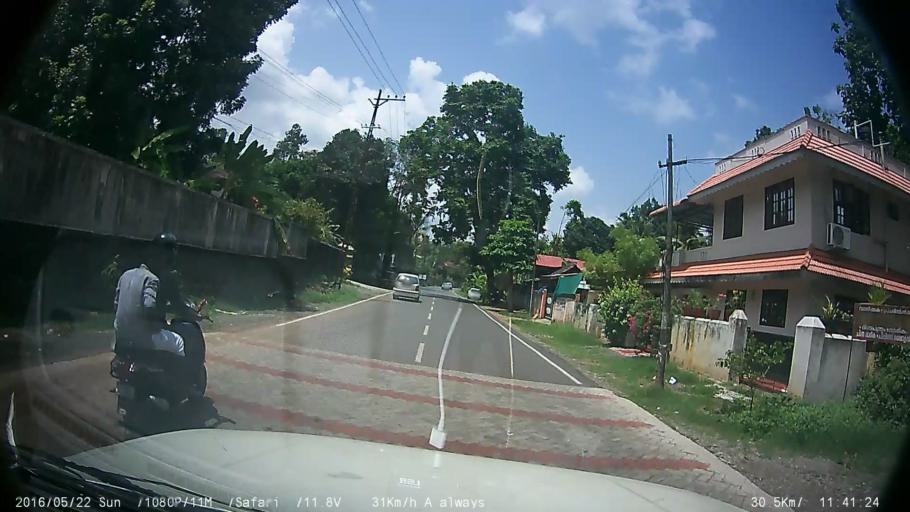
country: IN
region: Kerala
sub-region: Kottayam
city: Kottayam
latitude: 9.5486
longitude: 76.5187
